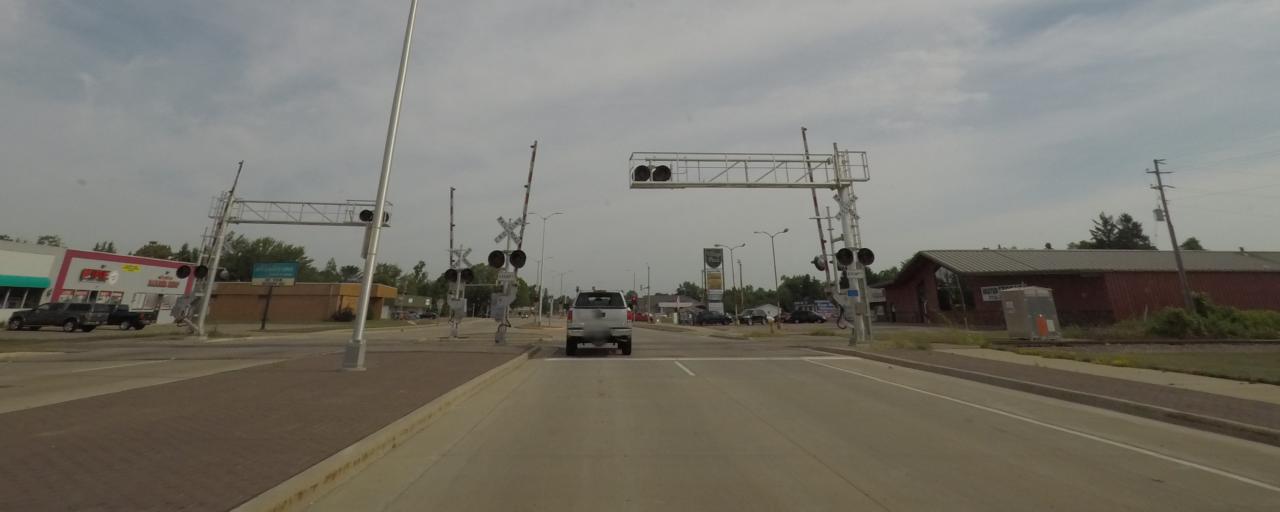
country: US
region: Wisconsin
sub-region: Portage County
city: Plover
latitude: 44.4568
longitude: -89.5436
